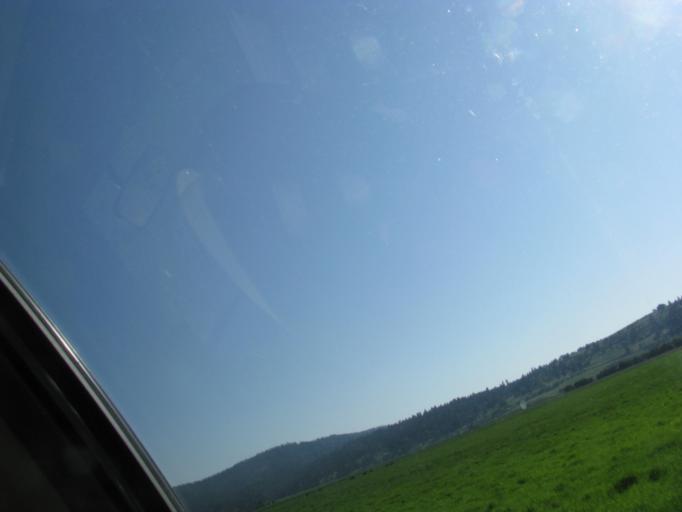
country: US
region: Washington
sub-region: Spokane County
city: Liberty Lake
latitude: 47.6249
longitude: -117.1140
